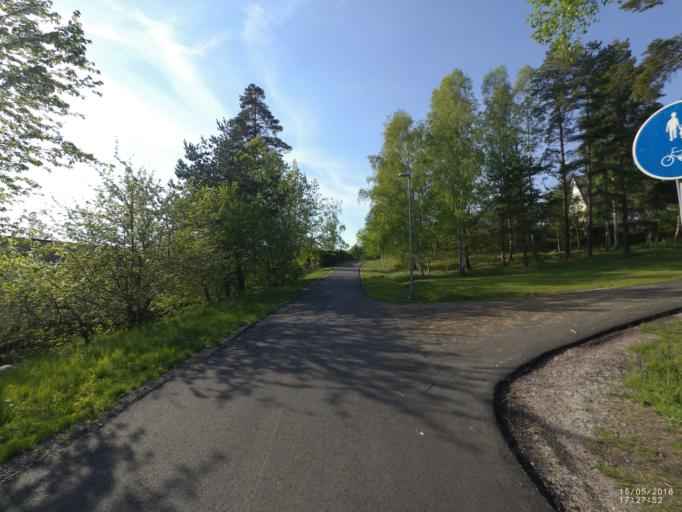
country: SE
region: Soedermanland
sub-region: Nykopings Kommun
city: Nykoping
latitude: 58.7261
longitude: 17.0250
